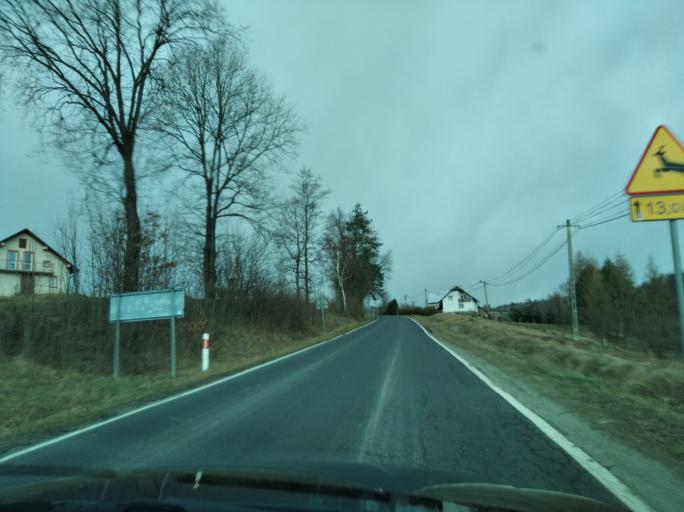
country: PL
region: Subcarpathian Voivodeship
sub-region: Powiat rzeszowski
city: Hyzne
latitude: 49.9115
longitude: 22.1998
